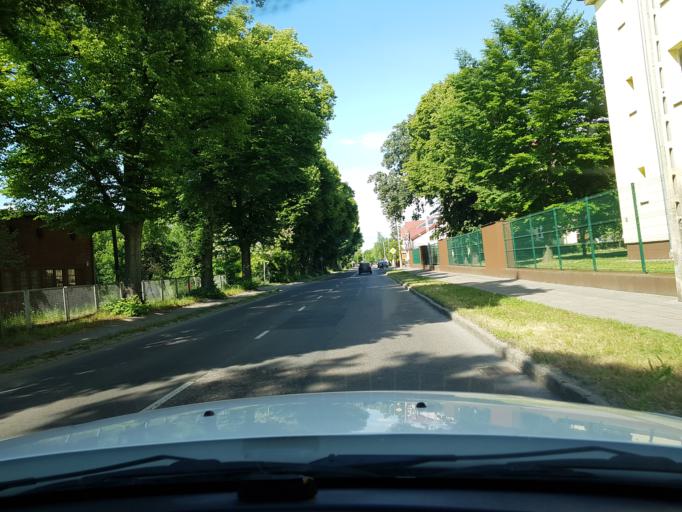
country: PL
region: West Pomeranian Voivodeship
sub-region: Szczecin
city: Szczecin
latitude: 53.3629
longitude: 14.5904
